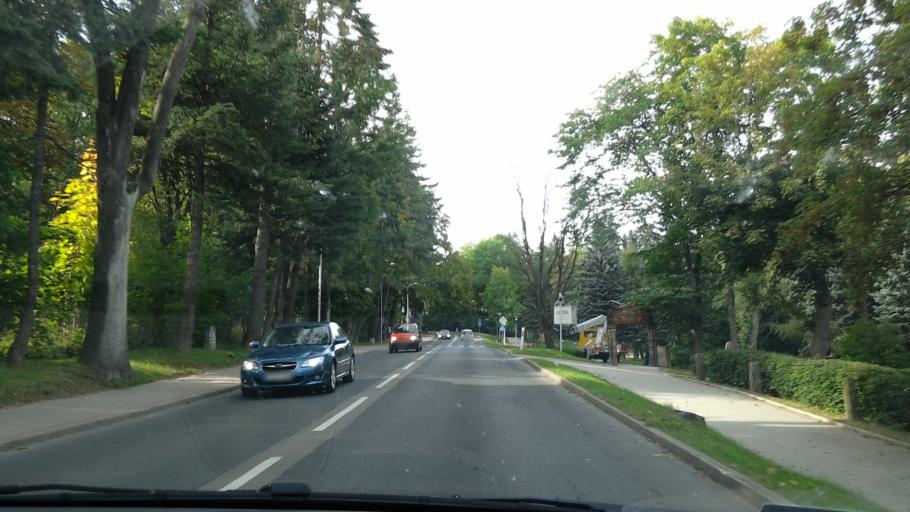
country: PL
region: Lower Silesian Voivodeship
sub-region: Powiat jeleniogorski
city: Karpacz
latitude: 50.7749
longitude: 15.7461
